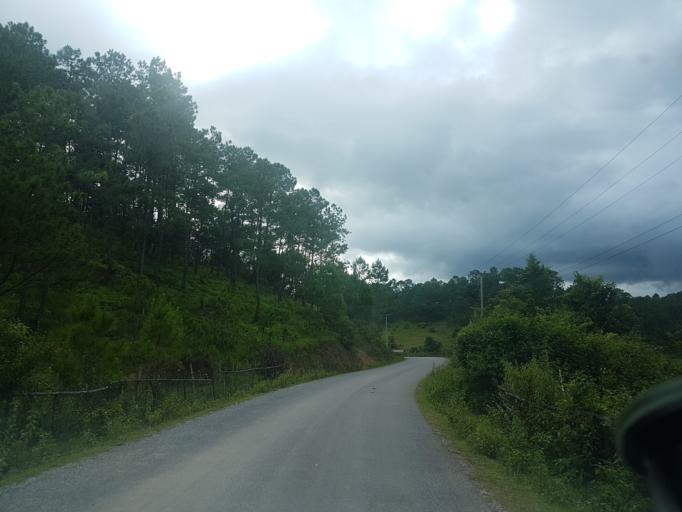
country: LA
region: Xiangkhoang
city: Muang Phonsavan
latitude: 19.5903
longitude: 103.2881
